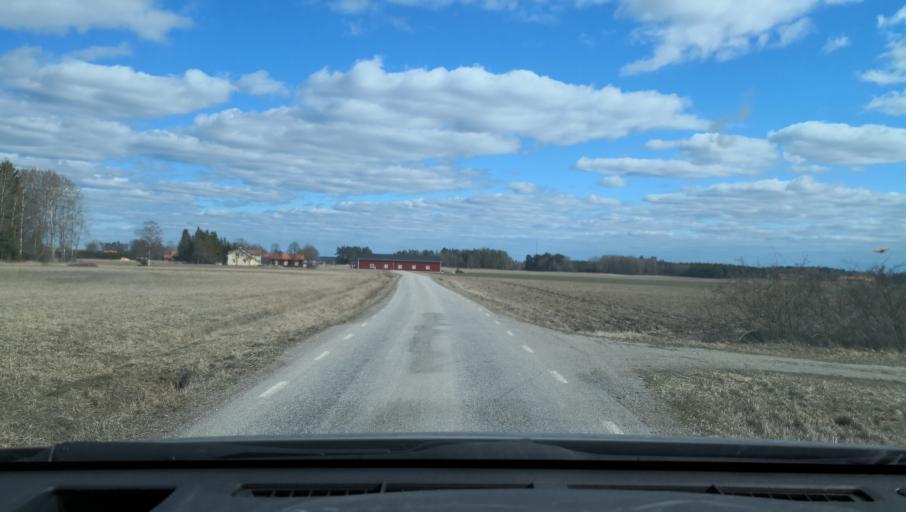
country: SE
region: Vaestmanland
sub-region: Sala Kommun
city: Sala
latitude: 59.8588
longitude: 16.6065
